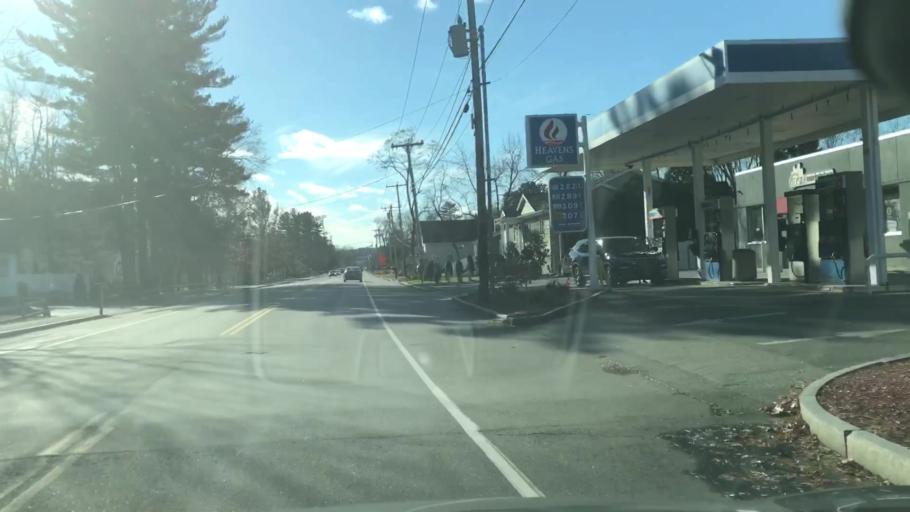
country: US
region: New Hampshire
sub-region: Hillsborough County
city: Bedford
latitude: 42.9662
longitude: -71.4912
